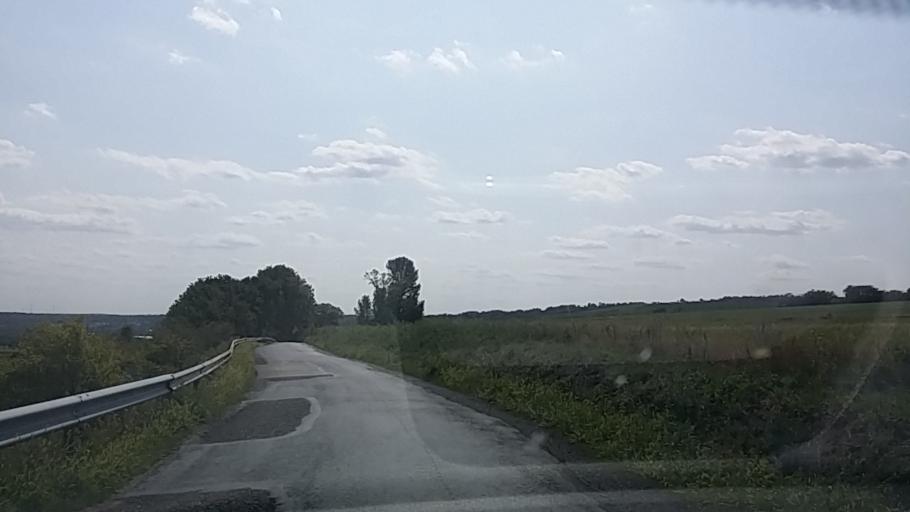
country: HU
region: Gyor-Moson-Sopron
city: Fertorakos
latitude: 47.6716
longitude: 16.6720
